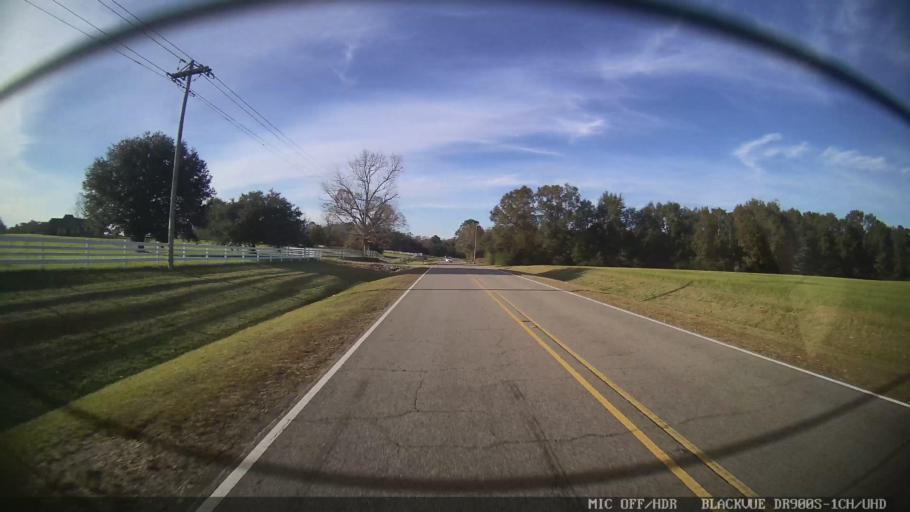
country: US
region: Mississippi
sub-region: Lamar County
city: Purvis
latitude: 31.1959
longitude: -89.2898
